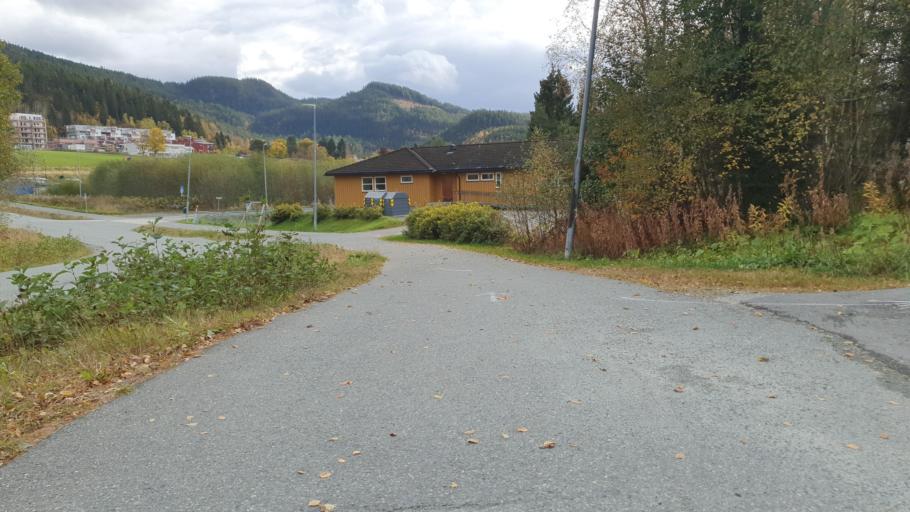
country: NO
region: Sor-Trondelag
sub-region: Klaebu
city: Klaebu
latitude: 63.3027
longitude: 10.4832
